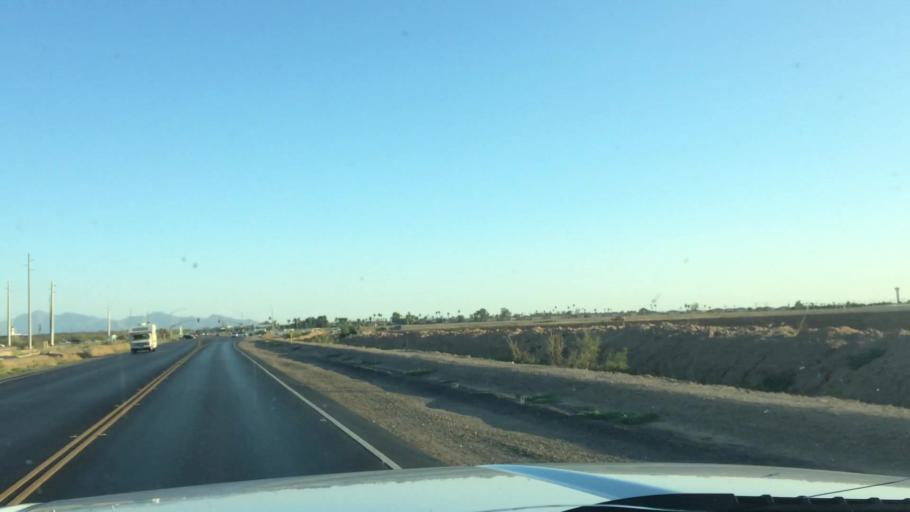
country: US
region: Arizona
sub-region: Maricopa County
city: Youngtown
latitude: 33.5542
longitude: -112.3417
